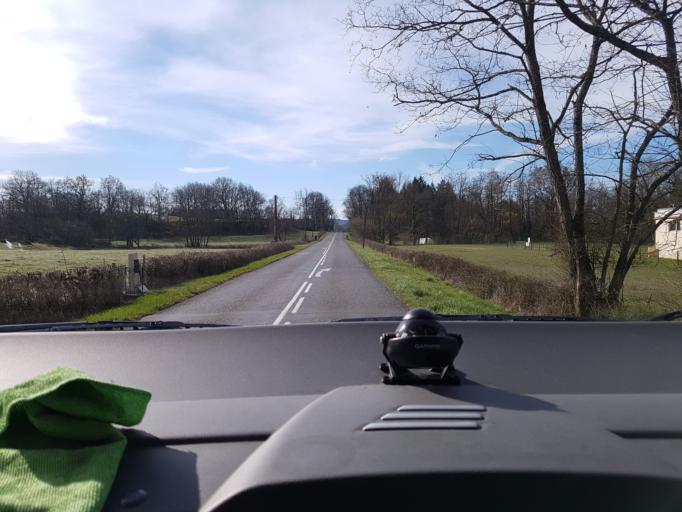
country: FR
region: Bourgogne
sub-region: Departement de Saone-et-Loire
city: Toulon-sur-Arroux
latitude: 46.7115
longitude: 4.1356
